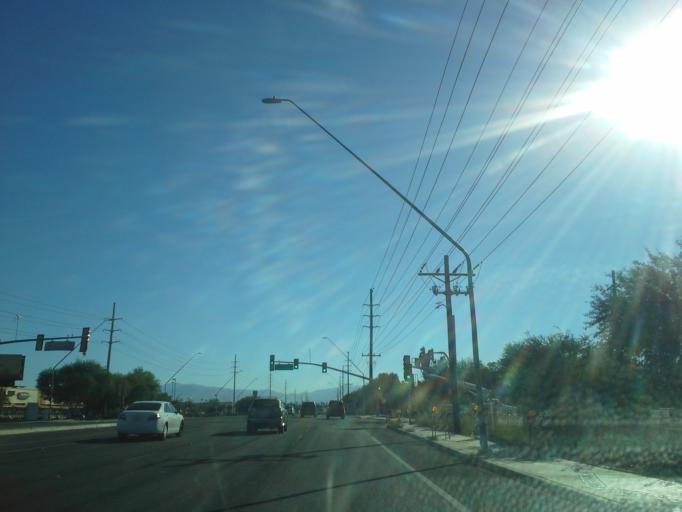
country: US
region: Arizona
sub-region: Pima County
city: Drexel Heights
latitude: 32.1337
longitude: -111.0040
